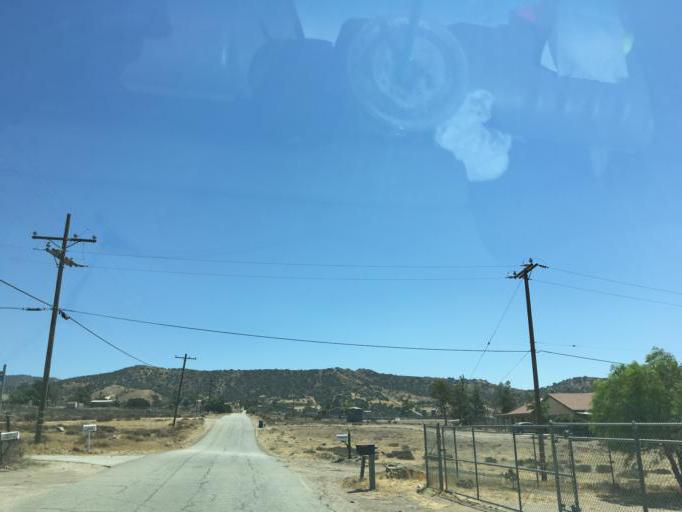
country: US
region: California
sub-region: Los Angeles County
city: Acton
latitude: 34.5244
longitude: -118.2294
